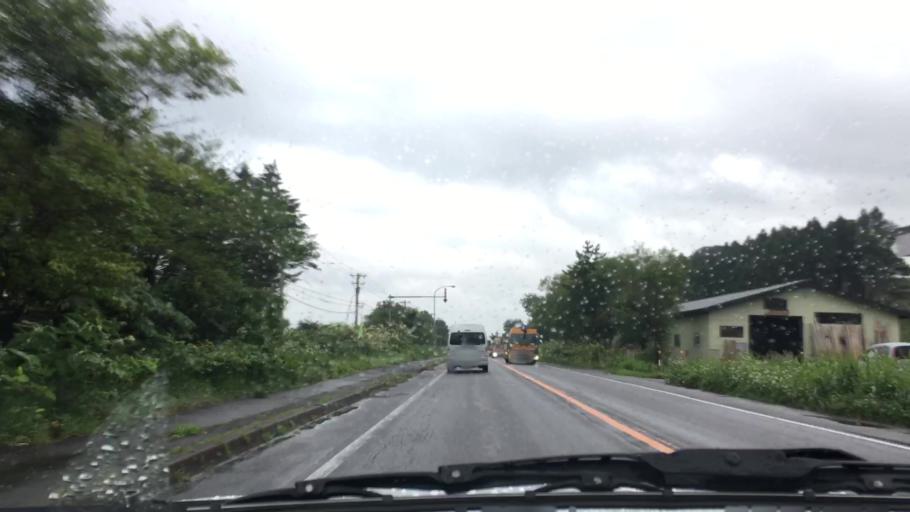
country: JP
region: Hokkaido
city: Nanae
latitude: 42.2239
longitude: 140.3531
